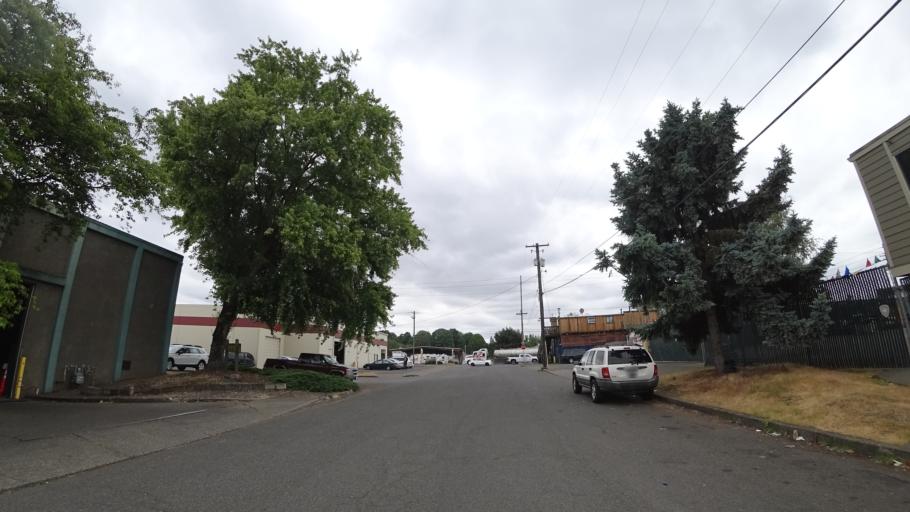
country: US
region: Washington
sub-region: Clark County
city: Vancouver
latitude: 45.5843
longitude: -122.6725
